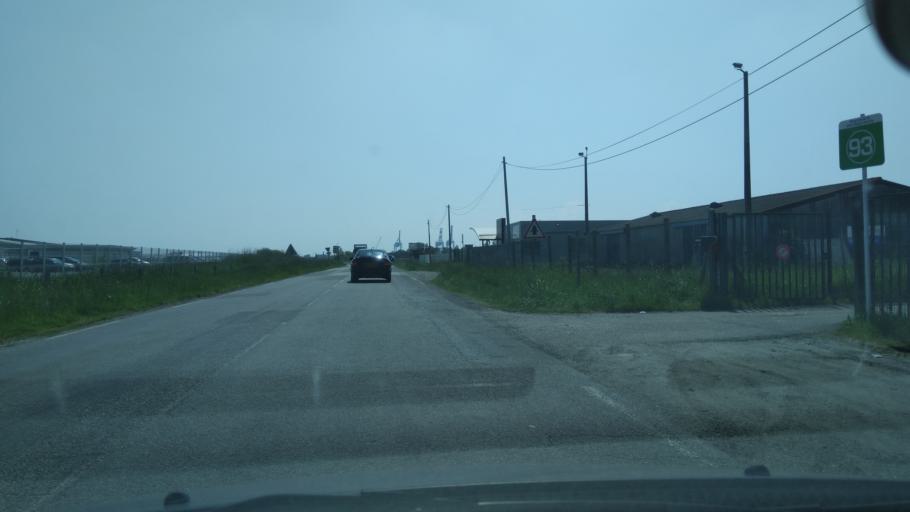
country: FR
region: Pays de la Loire
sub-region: Departement de la Loire-Atlantique
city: Trignac
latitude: 47.3106
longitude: -2.1747
